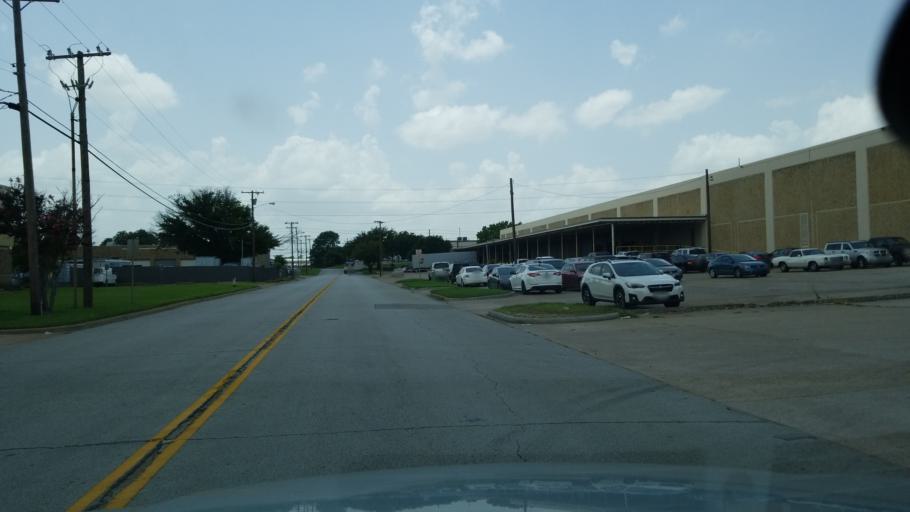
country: US
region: Texas
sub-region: Dallas County
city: Irving
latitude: 32.8184
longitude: -96.9143
